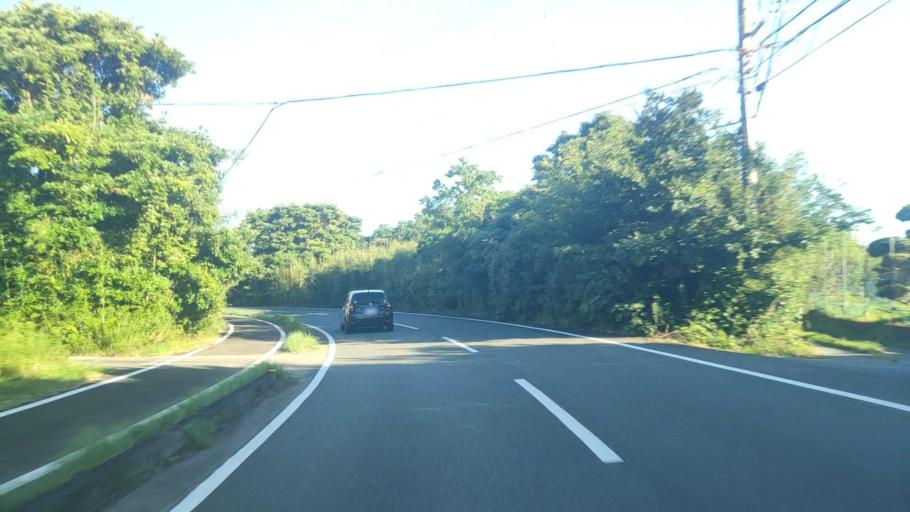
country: JP
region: Mie
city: Toba
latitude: 34.3289
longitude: 136.8725
